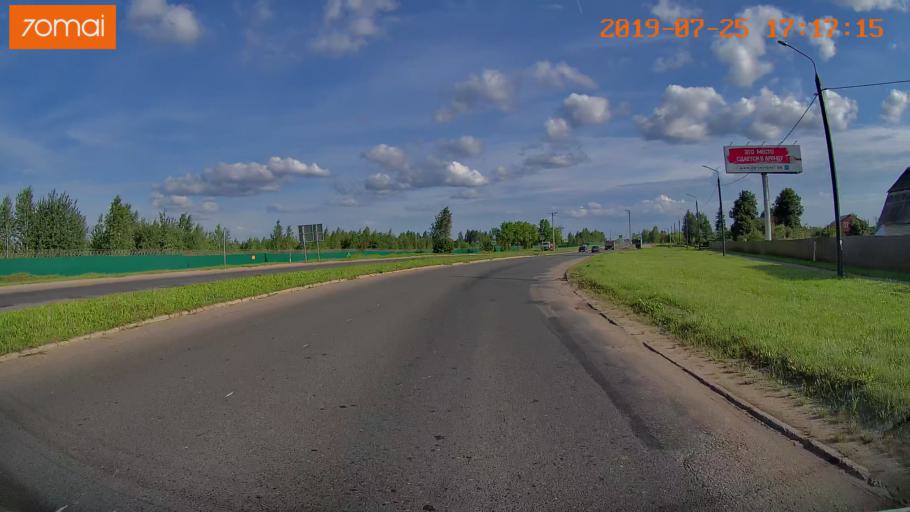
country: RU
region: Ivanovo
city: Bogorodskoye
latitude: 57.0574
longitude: 40.9624
